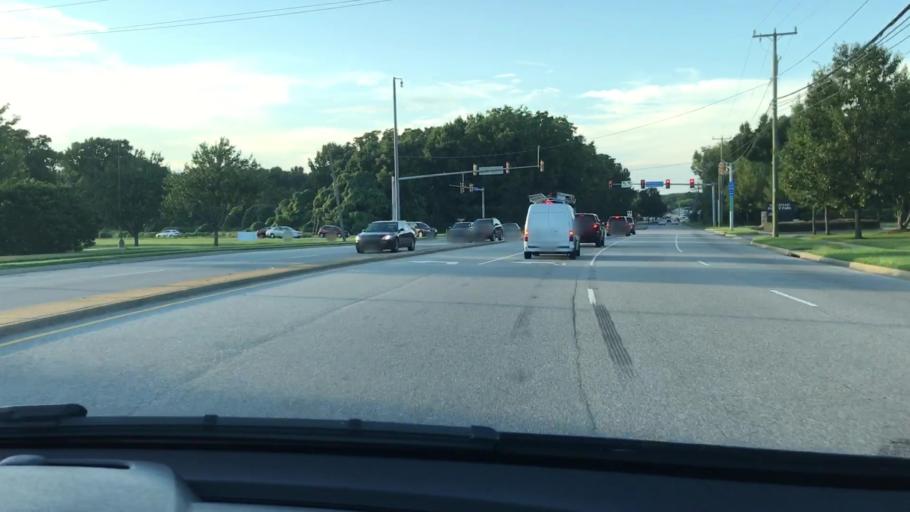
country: US
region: Virginia
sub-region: City of Hampton
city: Hampton
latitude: 37.0585
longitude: -76.3853
